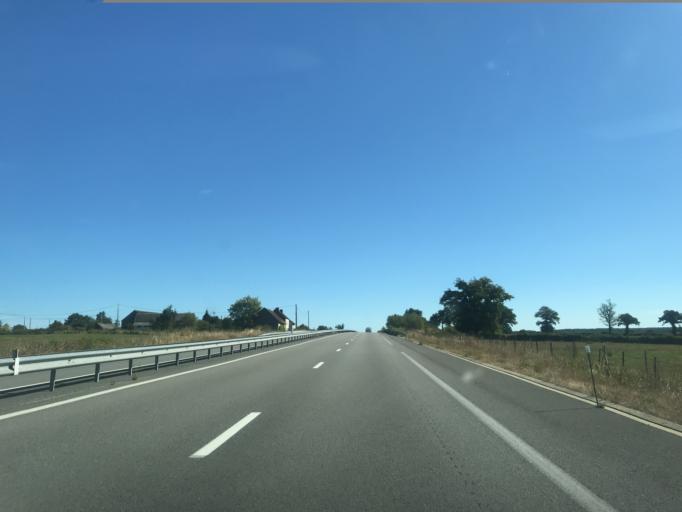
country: FR
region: Limousin
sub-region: Departement de la Creuse
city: Chambon-sur-Voueize
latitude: 46.2691
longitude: 2.3768
